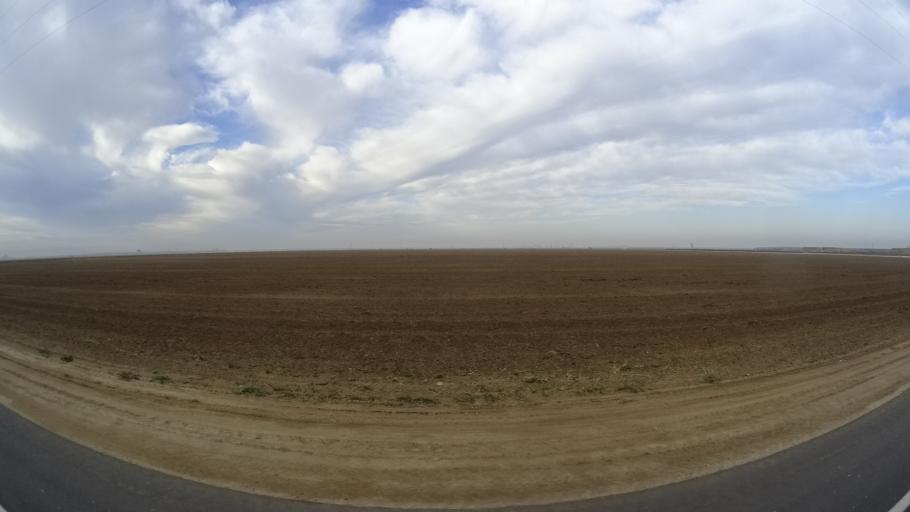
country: US
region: California
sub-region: Kern County
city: Rosedale
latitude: 35.4105
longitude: -119.1988
